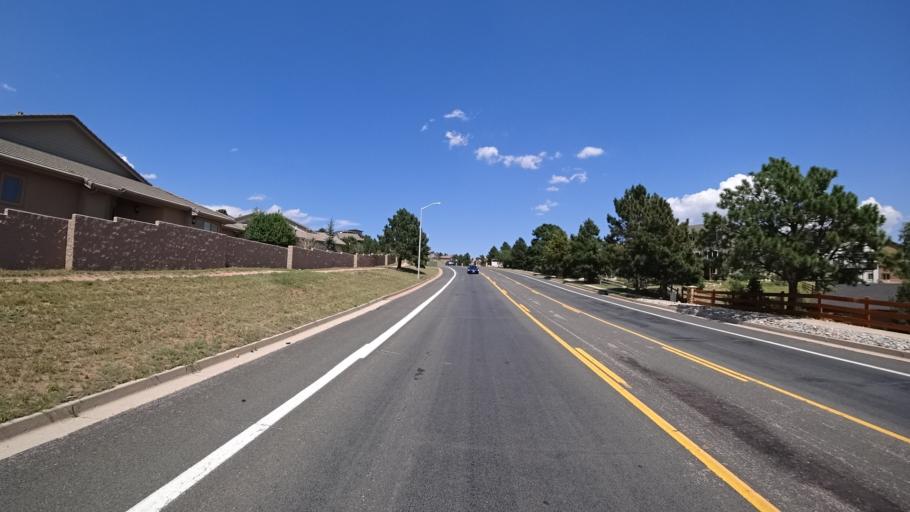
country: US
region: Colorado
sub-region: El Paso County
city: Manitou Springs
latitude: 38.9145
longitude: -104.8756
